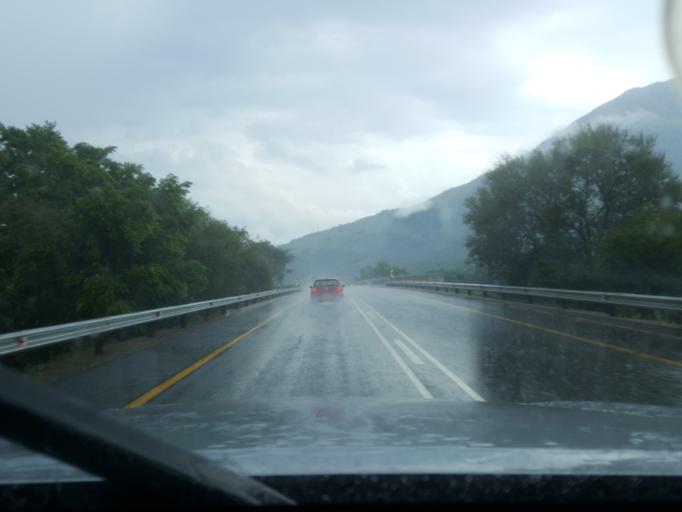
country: ZA
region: Mpumalanga
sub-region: Nkangala District Municipality
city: Belfast
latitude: -25.5983
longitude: 30.4548
